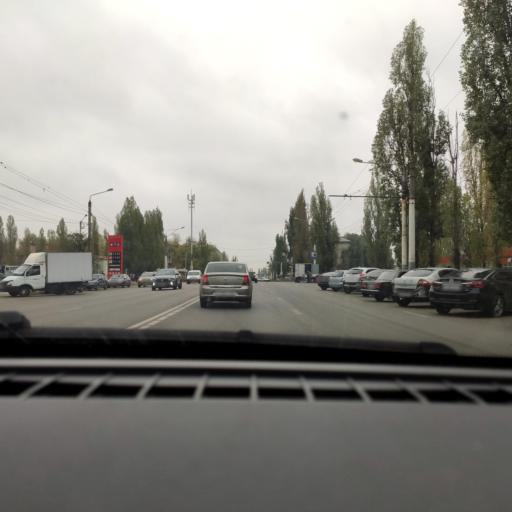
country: RU
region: Voronezj
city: Maslovka
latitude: 51.6114
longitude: 39.2373
